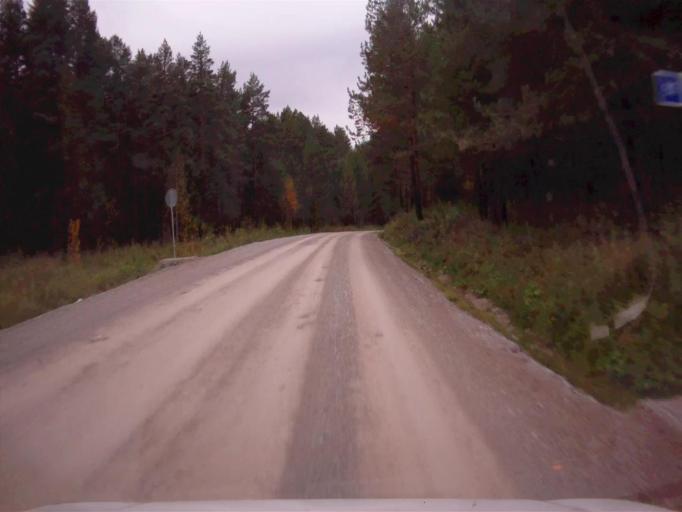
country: RU
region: Chelyabinsk
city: Nyazepetrovsk
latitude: 56.0455
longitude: 59.5196
